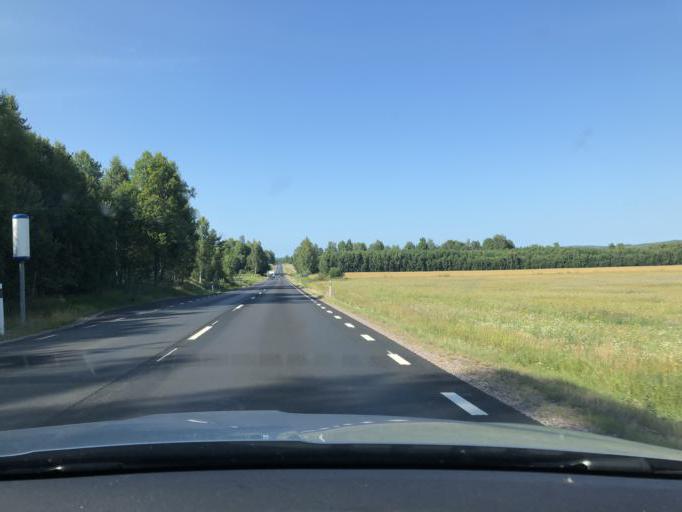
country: SE
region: Dalarna
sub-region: Hedemora Kommun
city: Hedemora
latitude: 60.3696
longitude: 15.9210
